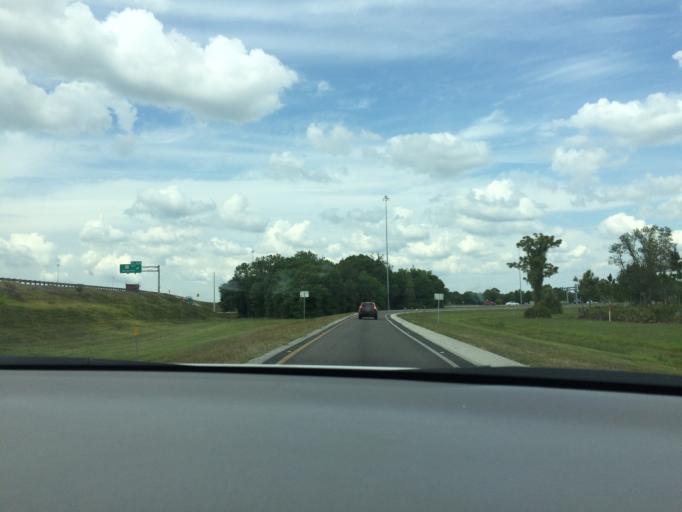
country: US
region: Florida
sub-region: Sarasota County
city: Desoto Lakes
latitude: 27.4386
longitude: -82.4587
